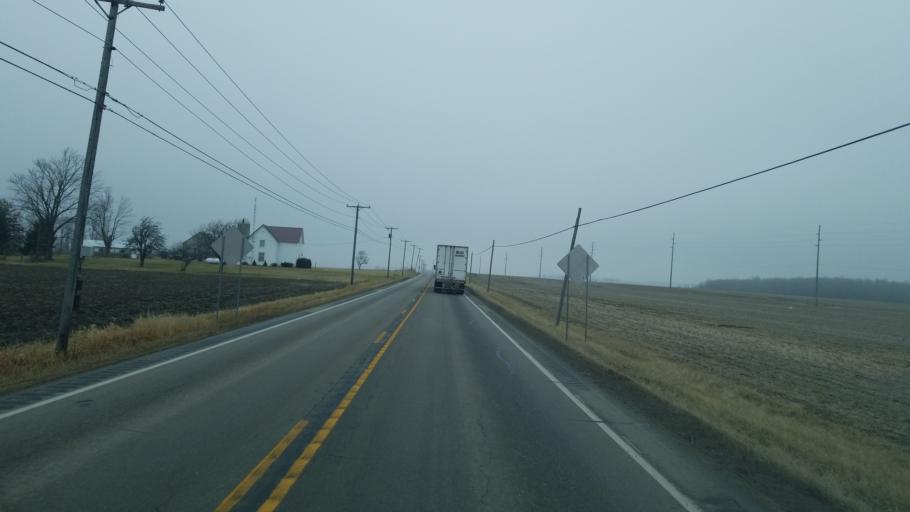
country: US
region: Indiana
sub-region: Adams County
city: Geneva
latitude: 40.5433
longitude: -84.9635
